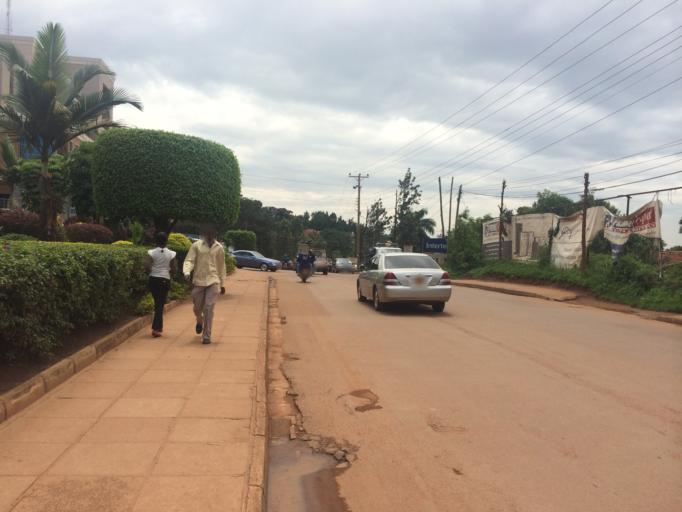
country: UG
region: Central Region
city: Kampala Central Division
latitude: 0.3371
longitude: 32.5869
